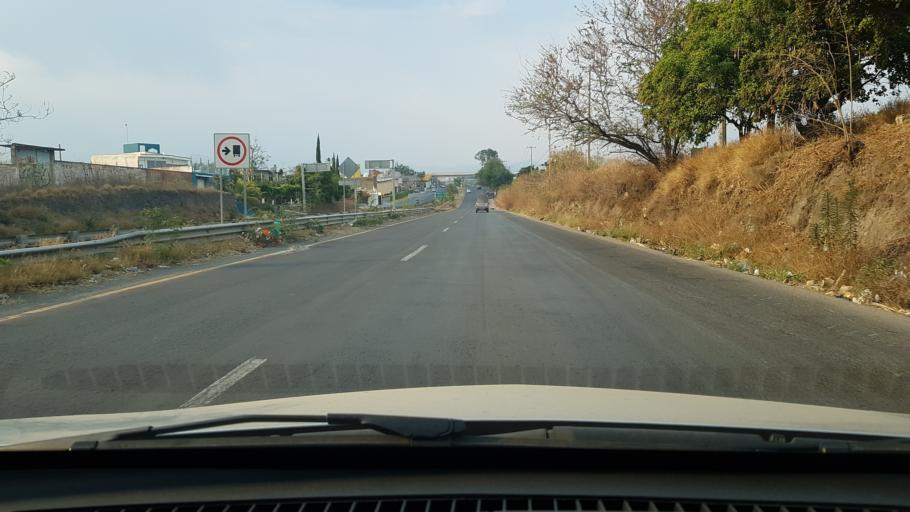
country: MX
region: Morelos
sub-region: Yecapixtla
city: Juan Morales
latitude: 18.8001
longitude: -98.9156
